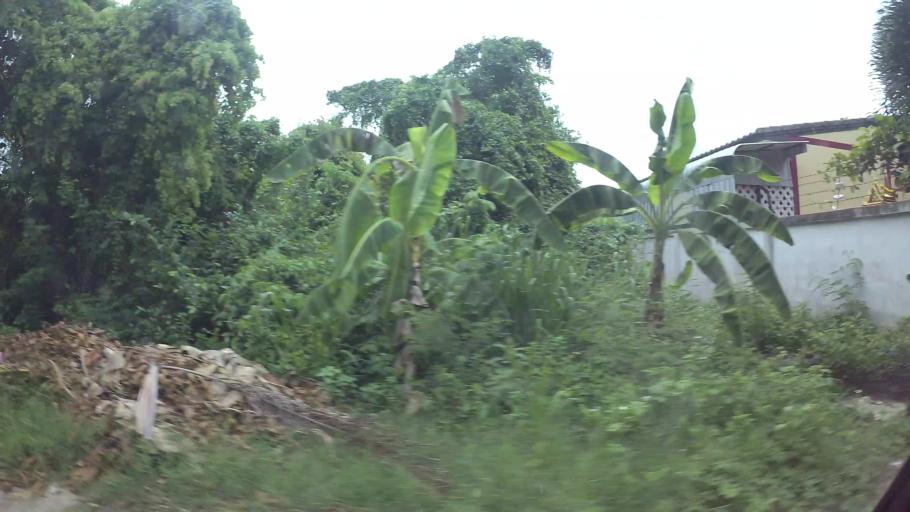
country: TH
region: Chon Buri
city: Sattahip
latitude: 12.6776
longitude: 100.9076
